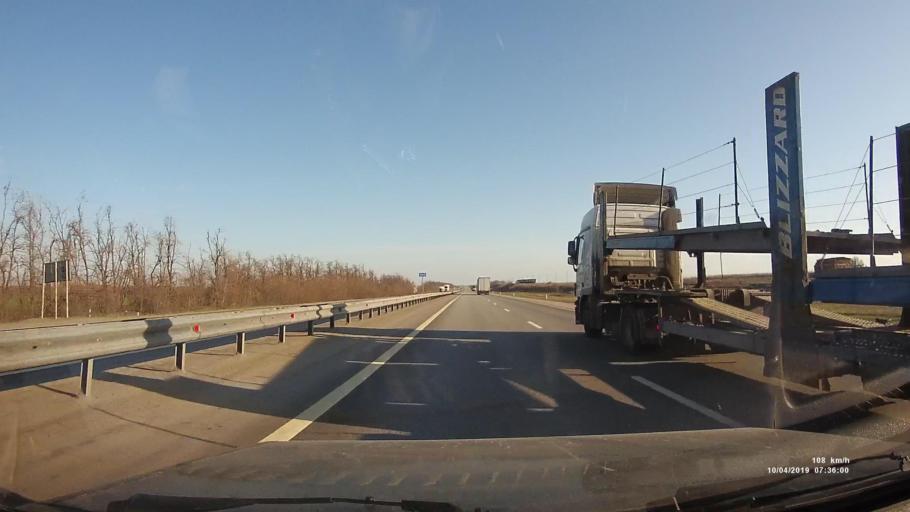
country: RU
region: Rostov
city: Likhoy
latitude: 48.0501
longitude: 40.2597
